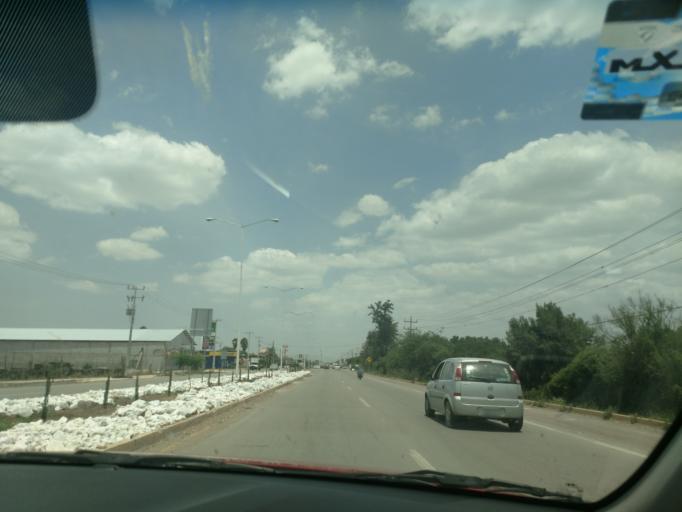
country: MX
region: San Luis Potosi
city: Ciudad Fernandez
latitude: 21.9378
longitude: -100.0321
